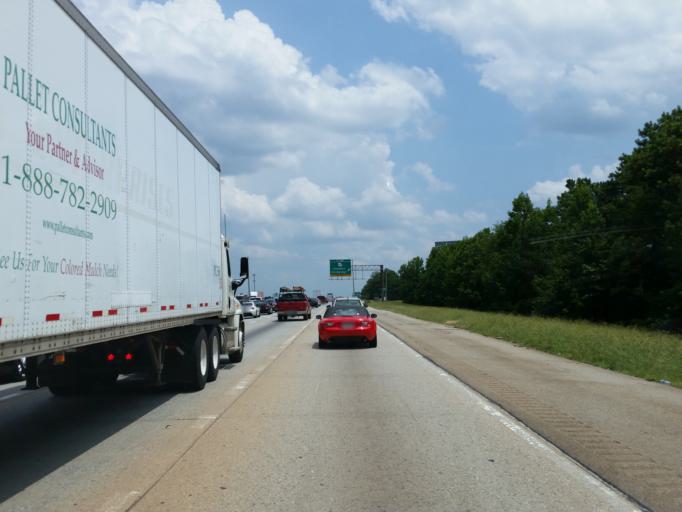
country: US
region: Georgia
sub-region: Henry County
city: Stockbridge
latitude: 33.5492
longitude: -84.2849
